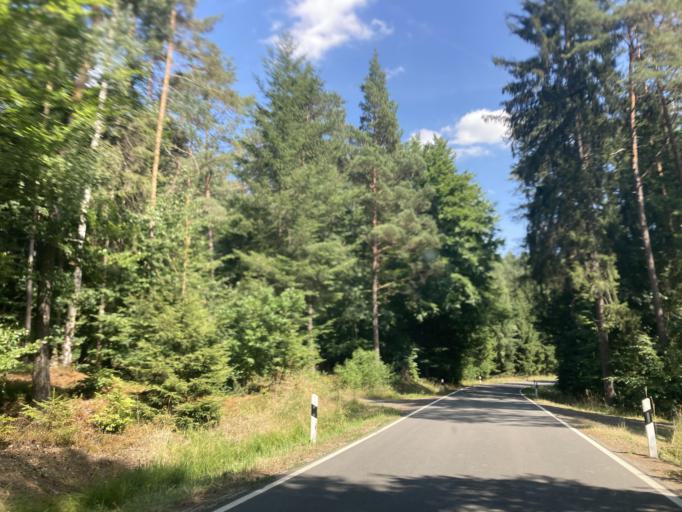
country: DE
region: Hesse
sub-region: Regierungsbezirk Kassel
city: Ottrau
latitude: 50.7288
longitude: 9.3930
